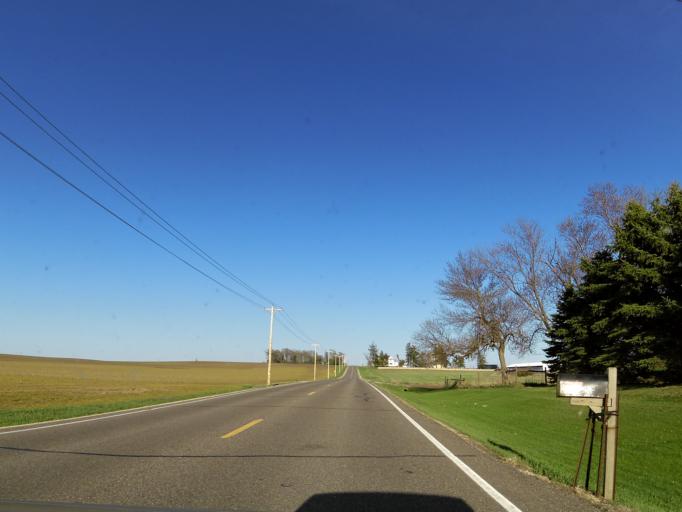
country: US
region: Minnesota
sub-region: Dakota County
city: Farmington
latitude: 44.5435
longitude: -93.0467
